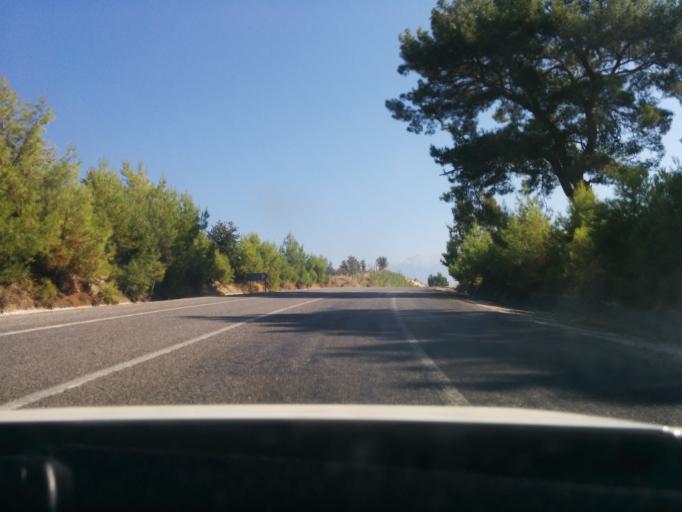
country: TR
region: Mugla
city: Esen
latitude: 36.4396
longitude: 29.2717
